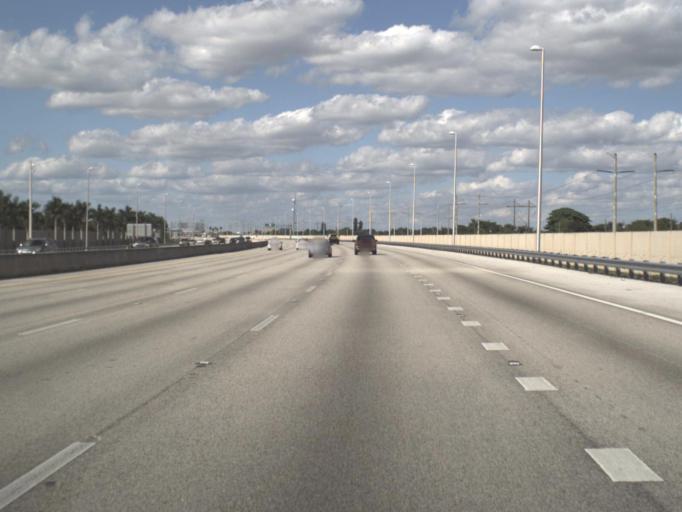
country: US
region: Florida
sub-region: Broward County
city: Lauderhill
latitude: 26.1244
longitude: -80.2174
